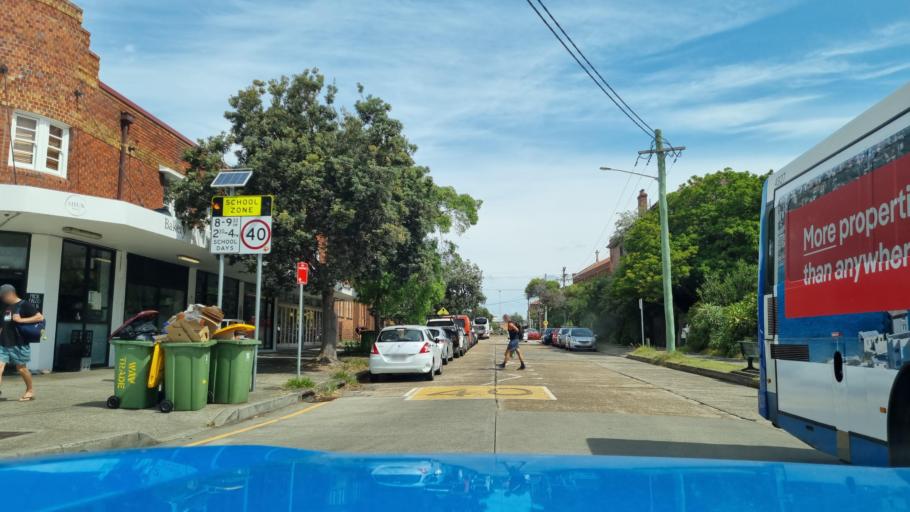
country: AU
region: New South Wales
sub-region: Waverley
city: North Bondi
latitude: -33.8839
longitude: 151.2763
